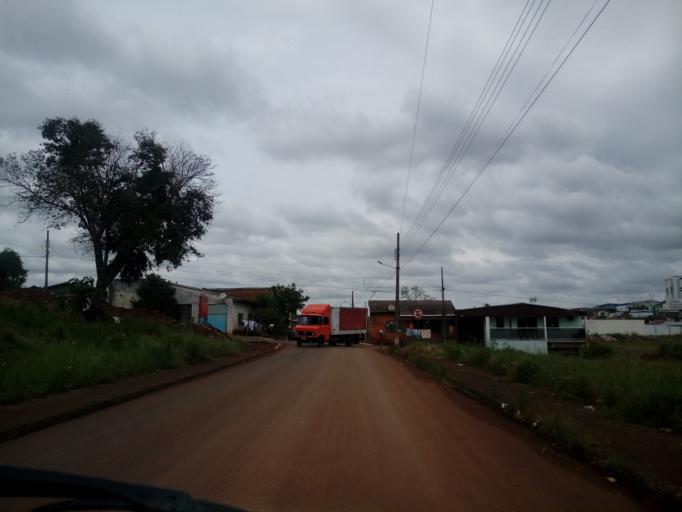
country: BR
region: Santa Catarina
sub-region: Chapeco
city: Chapeco
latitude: -27.0695
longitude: -52.6197
